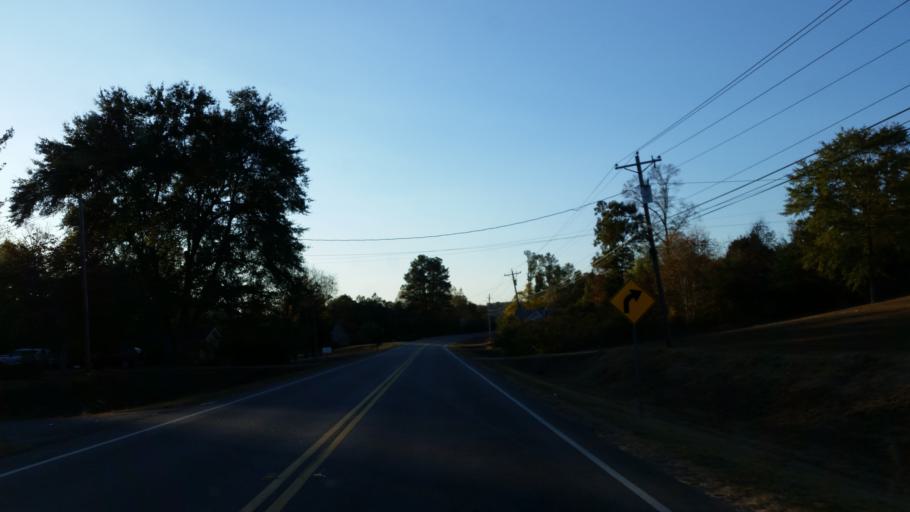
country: US
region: Georgia
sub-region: Gordon County
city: Calhoun
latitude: 34.5174
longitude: -84.9635
